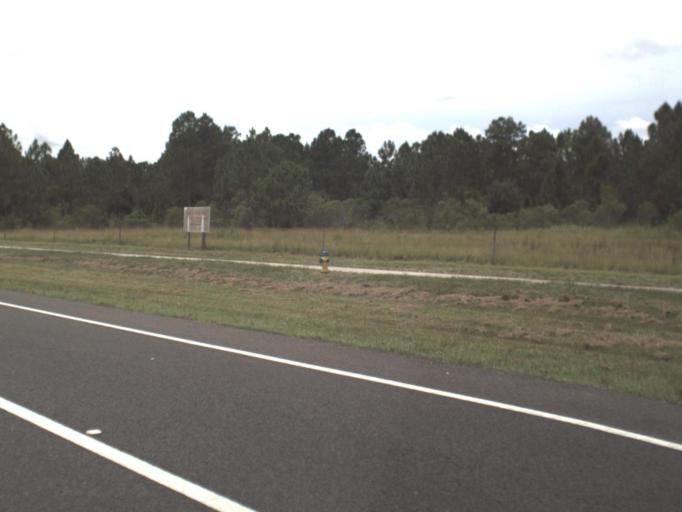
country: US
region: Florida
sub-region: Hillsborough County
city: Pebble Creek
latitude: 28.1897
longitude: -82.3426
